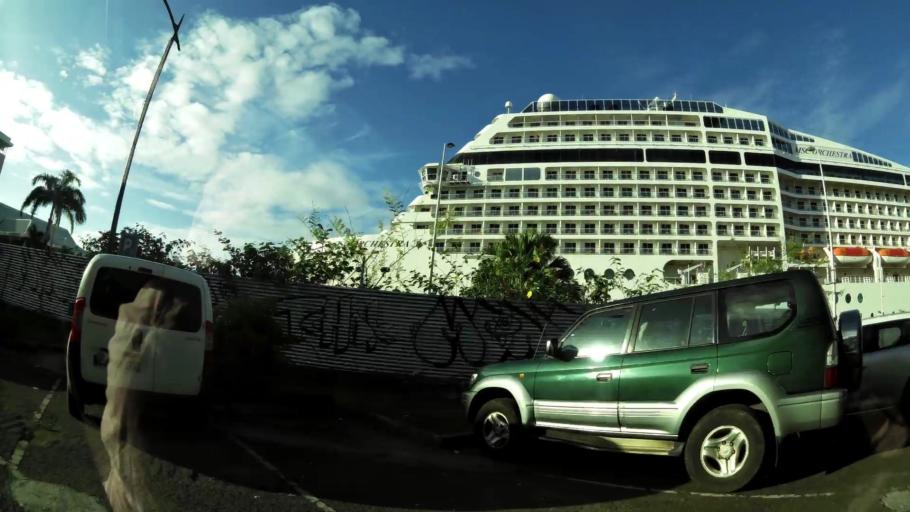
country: GP
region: Guadeloupe
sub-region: Guadeloupe
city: Pointe-a-Pitre
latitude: 16.2356
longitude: -61.5377
